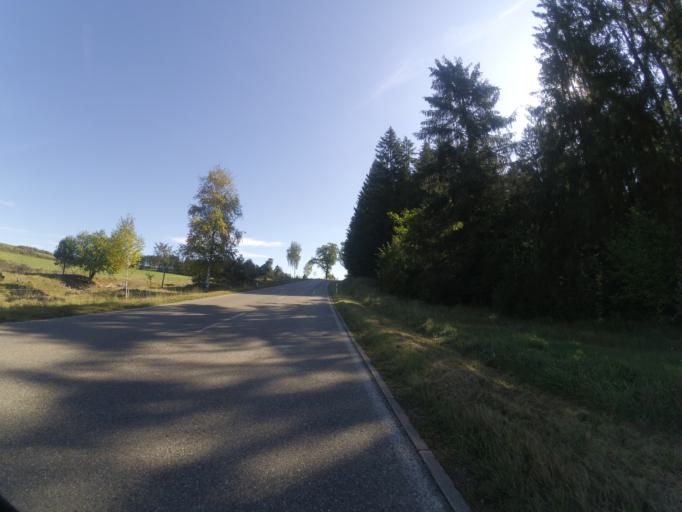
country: DE
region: Baden-Wuerttemberg
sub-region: Tuebingen Region
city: Borslingen
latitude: 48.5459
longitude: 10.0494
